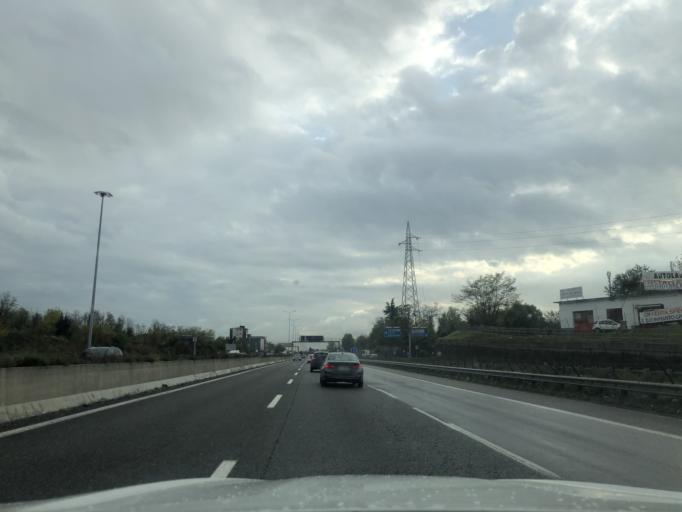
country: IT
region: Lombardy
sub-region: Provincia di Monza e Brianza
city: Santa Margherita
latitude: 45.6210
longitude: 9.2242
